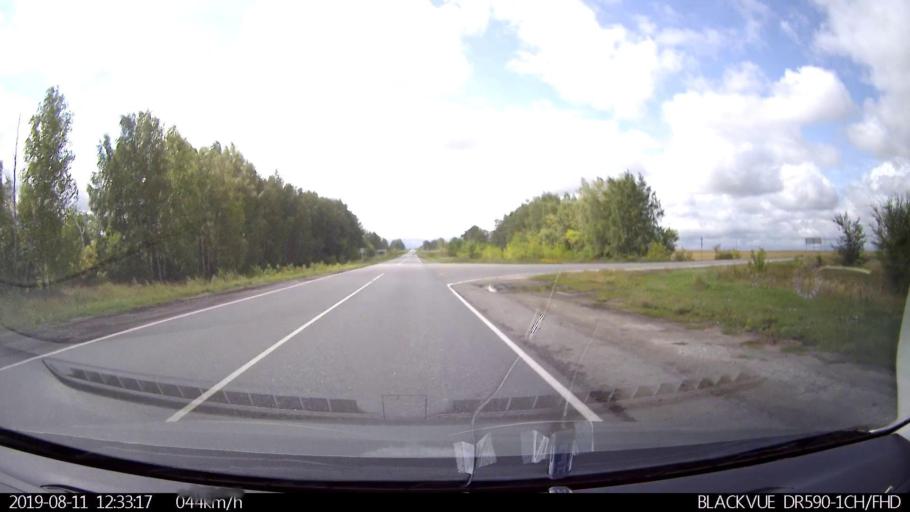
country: RU
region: Ulyanovsk
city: Ignatovka
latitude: 53.8095
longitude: 47.8563
